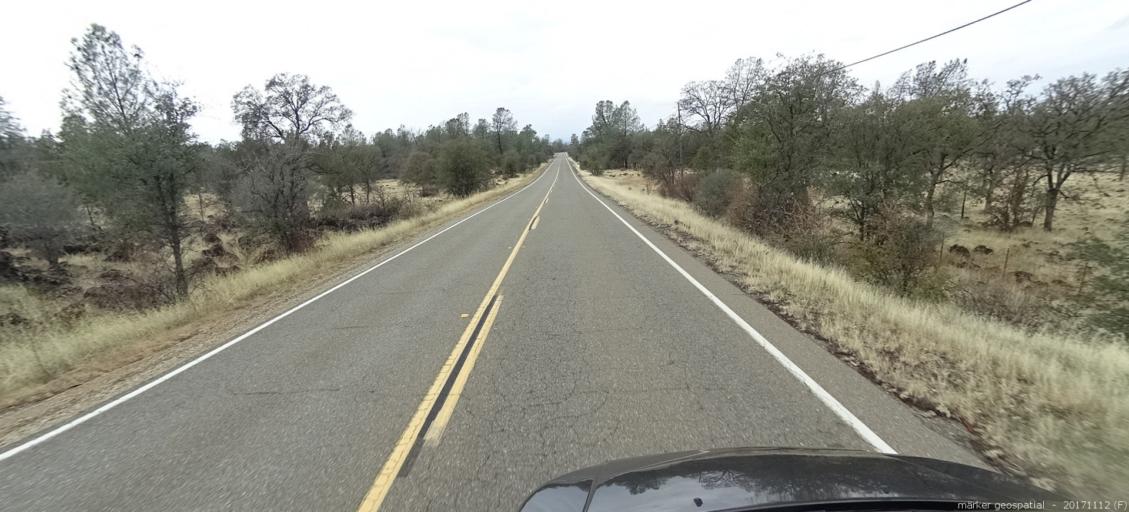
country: US
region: California
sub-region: Shasta County
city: Palo Cedro
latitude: 40.4811
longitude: -122.0947
